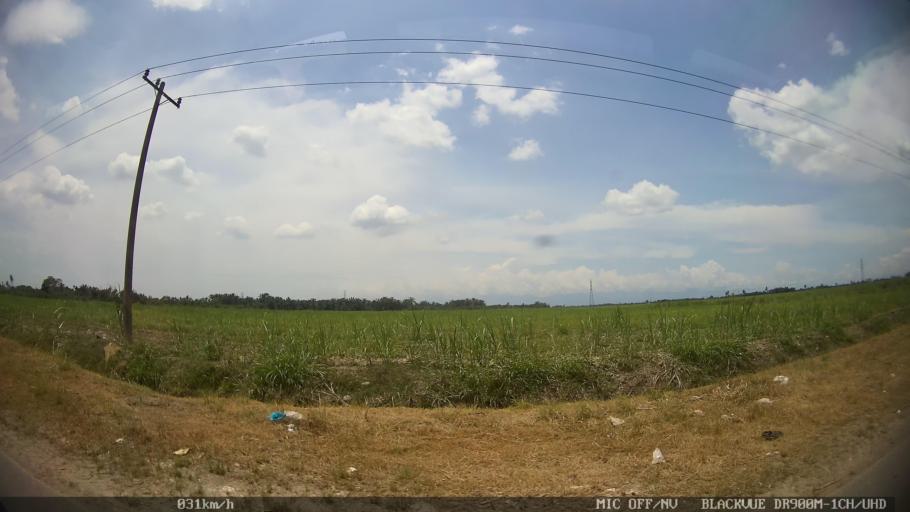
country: ID
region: North Sumatra
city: Binjai
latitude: 3.5895
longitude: 98.5440
